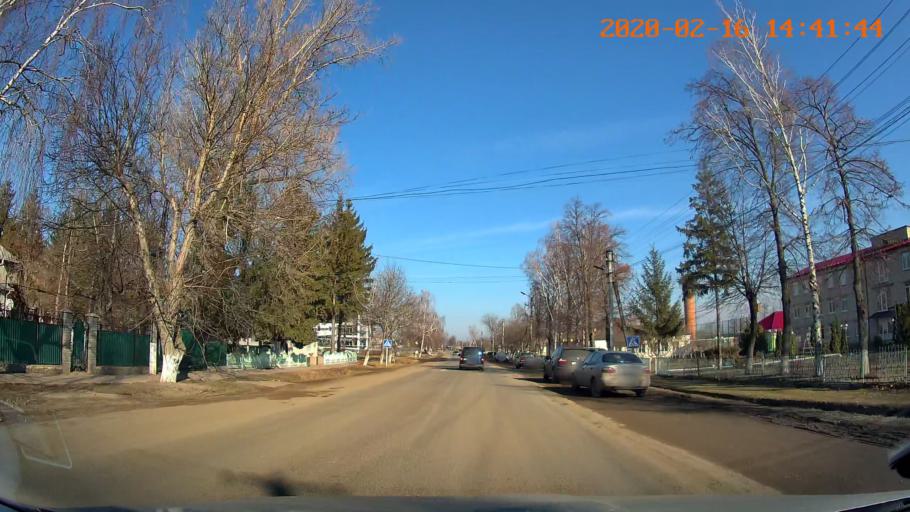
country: RO
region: Botosani
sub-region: Comuna Darabani
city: Bajura
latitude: 48.2547
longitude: 26.5759
